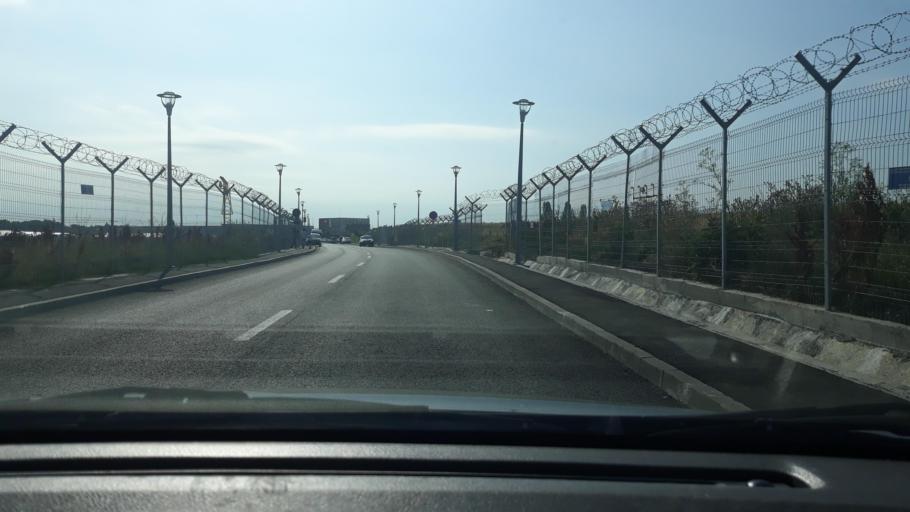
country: RO
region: Bihor
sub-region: Comuna Biharea
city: Oradea
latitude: 47.0394
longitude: 21.9059
